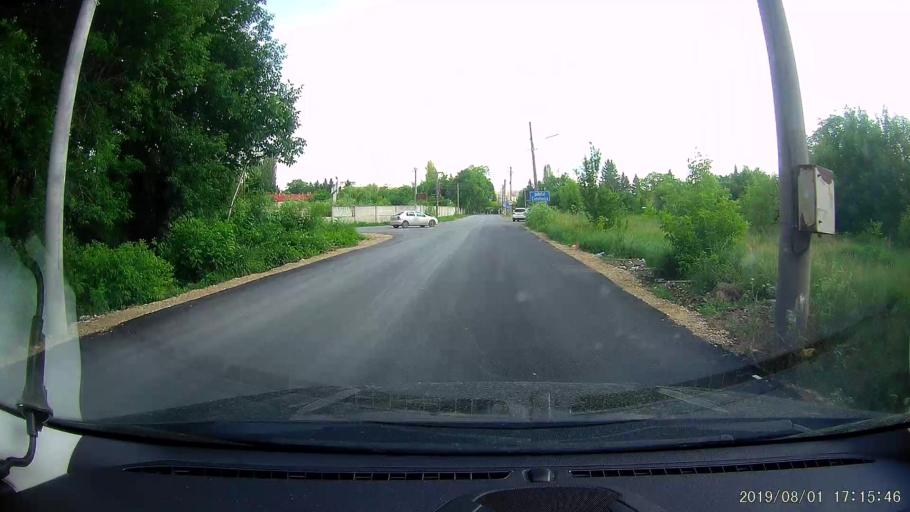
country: BG
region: Silistra
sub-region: Obshtina Silistra
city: Silistra
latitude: 44.1193
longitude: 27.2771
